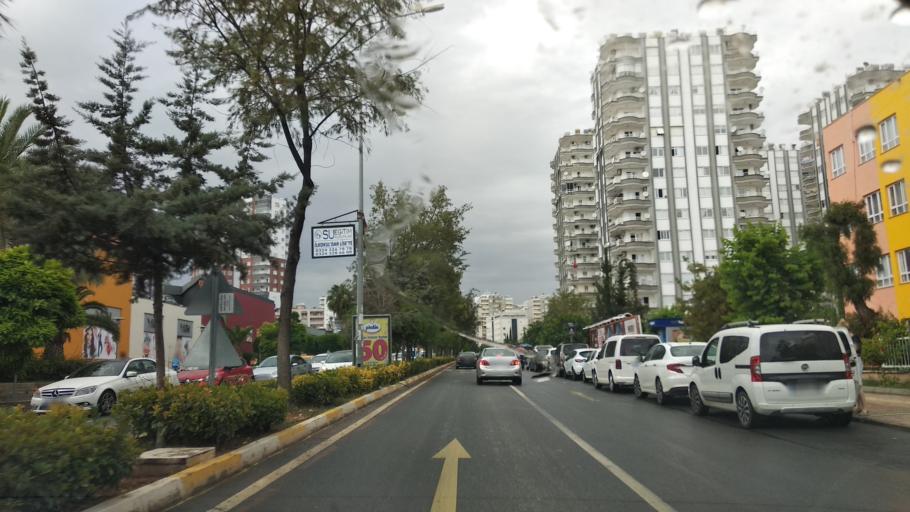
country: TR
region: Mersin
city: Mercin
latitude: 36.7857
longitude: 34.5891
